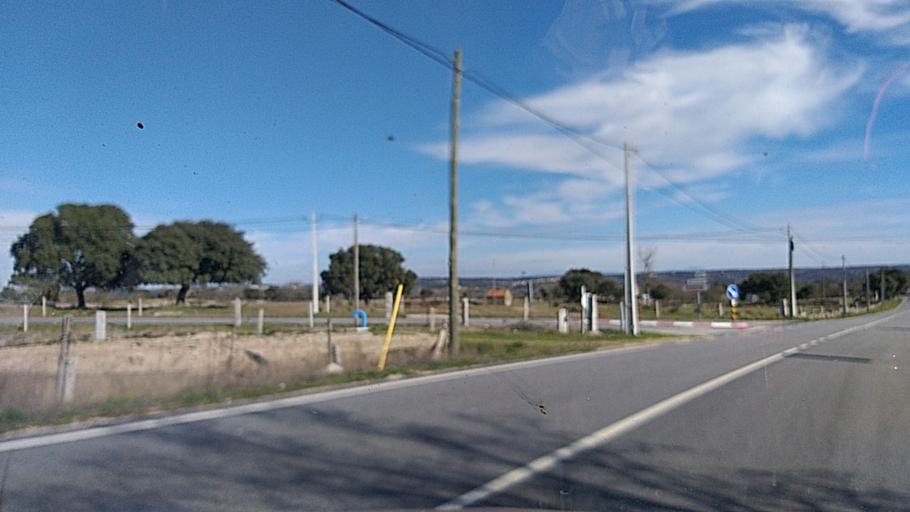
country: ES
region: Castille and Leon
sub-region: Provincia de Salamanca
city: Fuentes de Onoro
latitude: 40.6025
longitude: -6.9481
